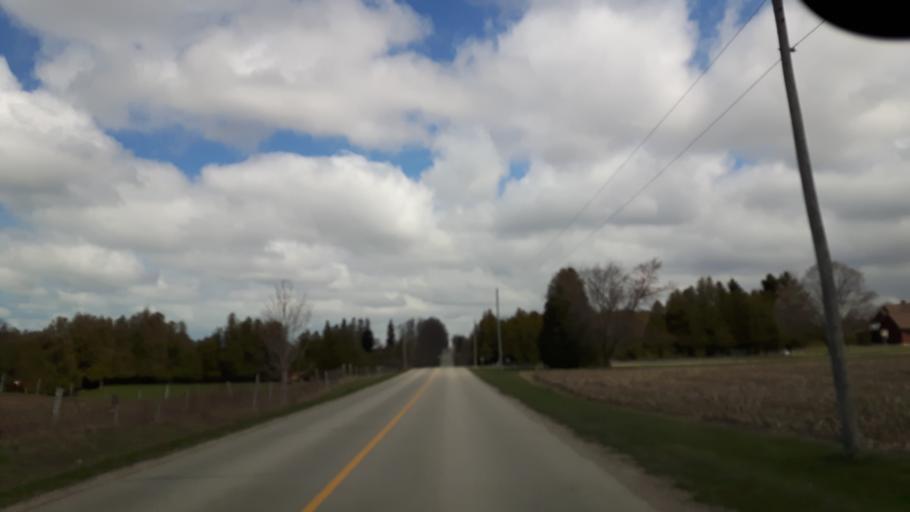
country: CA
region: Ontario
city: Goderich
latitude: 43.6654
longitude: -81.6846
